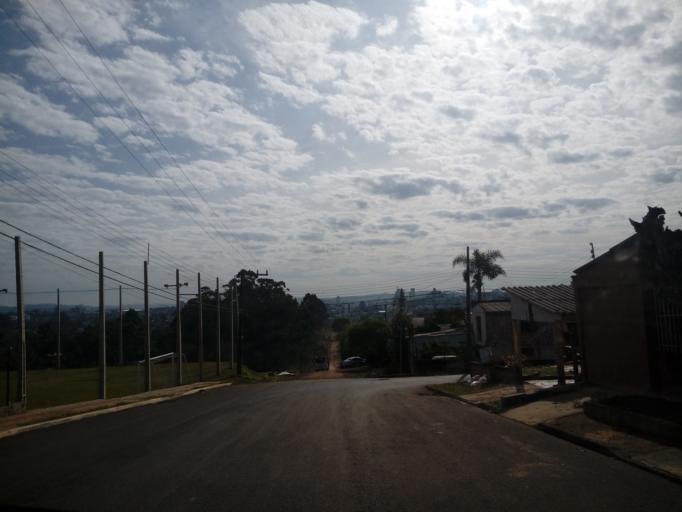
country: BR
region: Santa Catarina
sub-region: Chapeco
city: Chapeco
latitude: -27.1187
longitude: -52.6300
